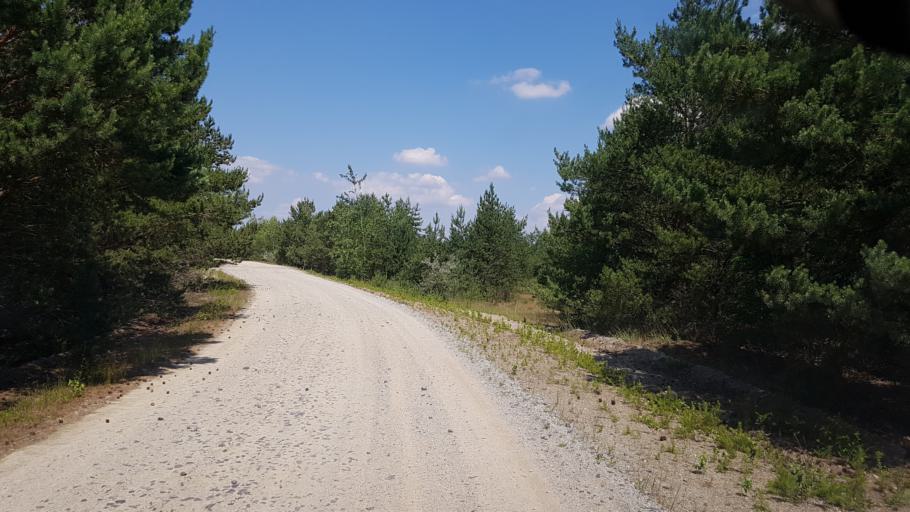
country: DE
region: Brandenburg
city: Lauchhammer
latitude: 51.5557
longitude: 13.7822
